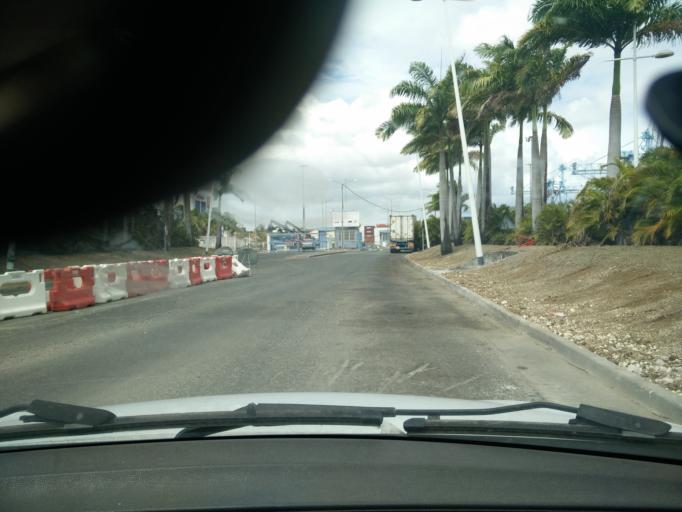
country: GP
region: Guadeloupe
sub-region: Guadeloupe
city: Pointe-a-Pitre
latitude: 16.2275
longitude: -61.5497
